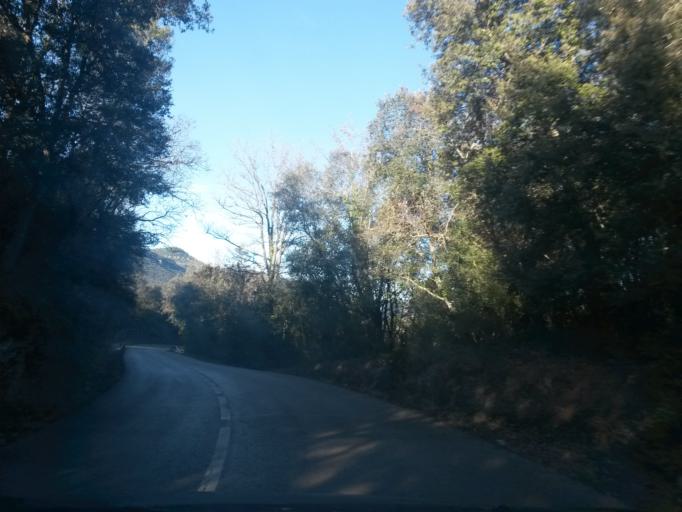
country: ES
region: Catalonia
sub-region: Provincia de Girona
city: la Cellera de Ter
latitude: 42.0228
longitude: 2.6687
